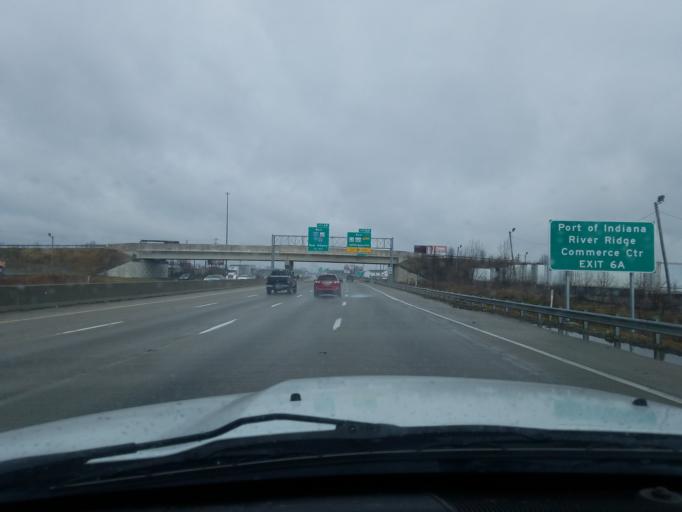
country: US
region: Indiana
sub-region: Clark County
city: Clarksville
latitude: 38.3346
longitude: -85.7536
